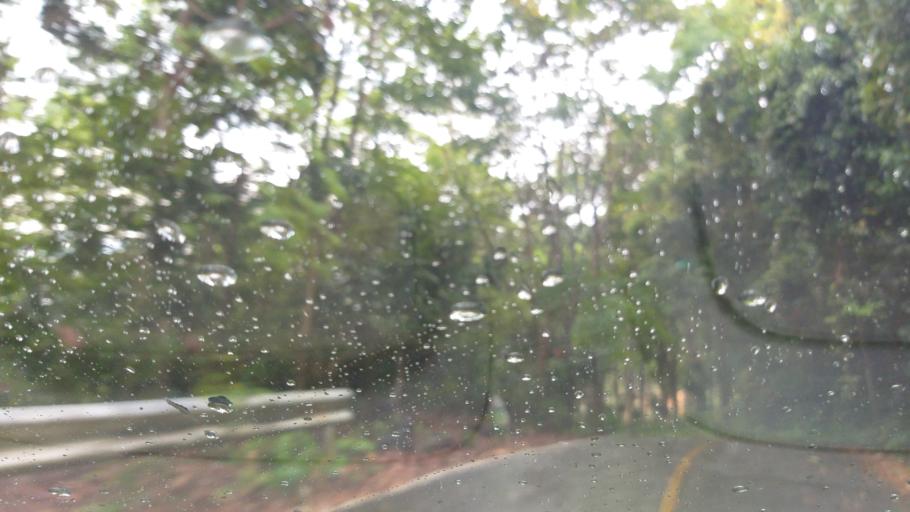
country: TH
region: Trat
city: Ko Chang Tai
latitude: 11.9771
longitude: 102.3224
